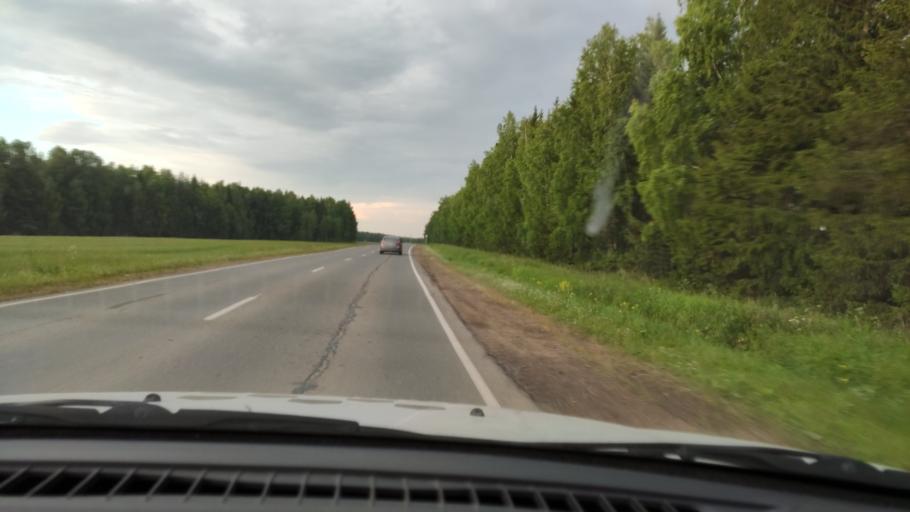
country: RU
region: Perm
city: Kukushtan
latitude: 57.4719
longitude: 56.5649
